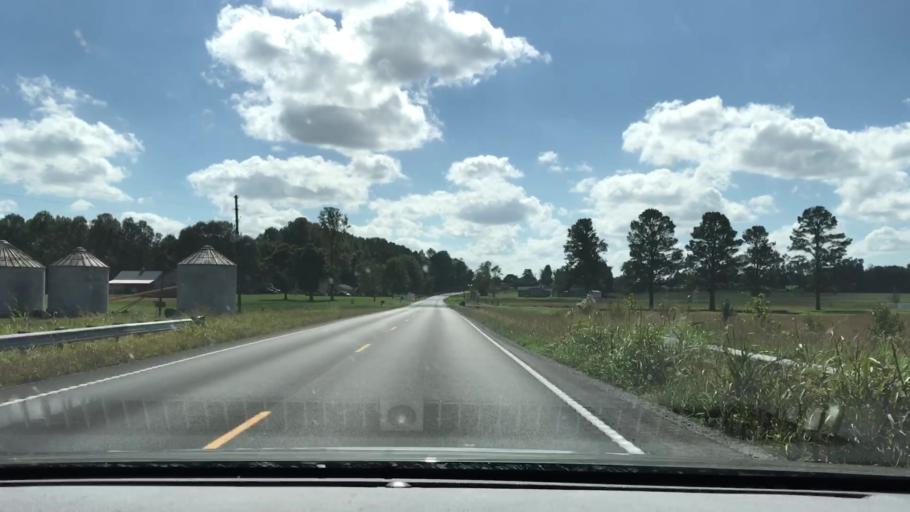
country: US
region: Kentucky
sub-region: Graves County
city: Mayfield
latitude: 36.8601
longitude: -88.5721
